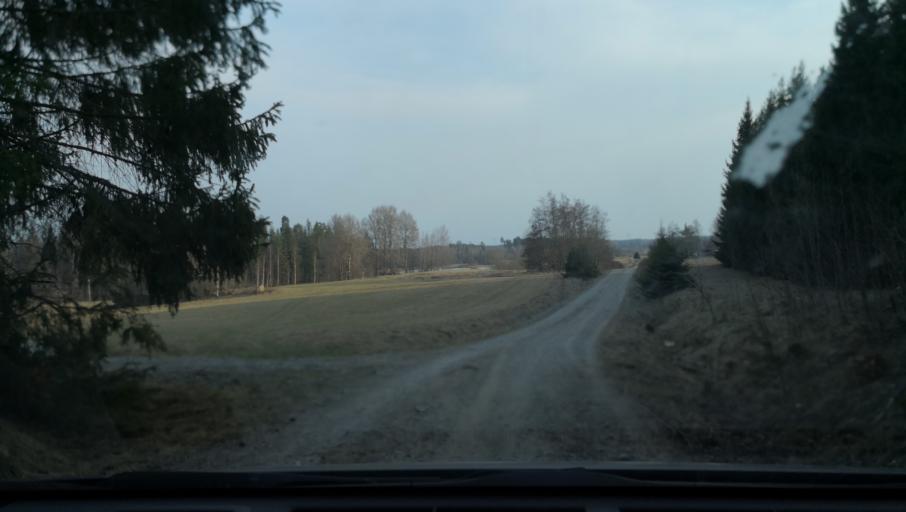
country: SE
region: OErebro
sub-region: Orebro Kommun
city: Hovsta
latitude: 59.3930
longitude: 15.2710
